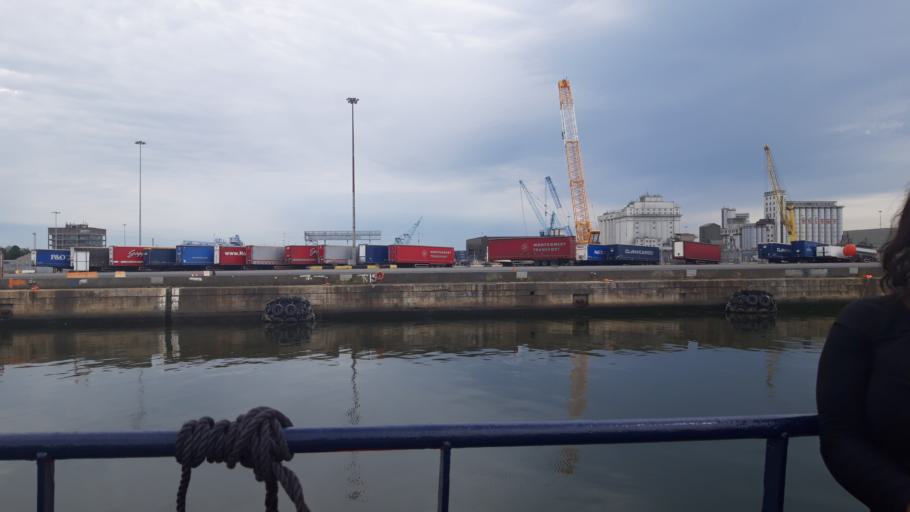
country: IE
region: Leinster
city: Ringsend
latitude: 53.3457
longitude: -6.2236
